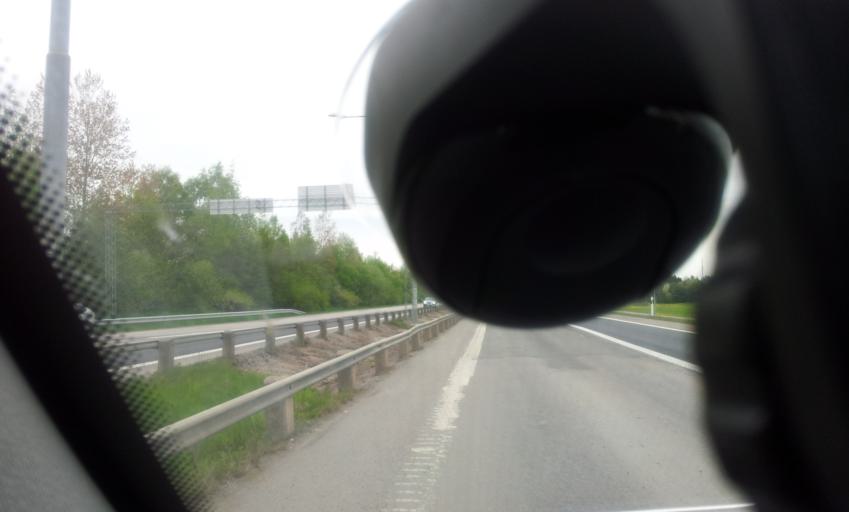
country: SE
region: OEstergoetland
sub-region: Norrkopings Kommun
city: Norrkoping
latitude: 58.5576
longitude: 16.2319
